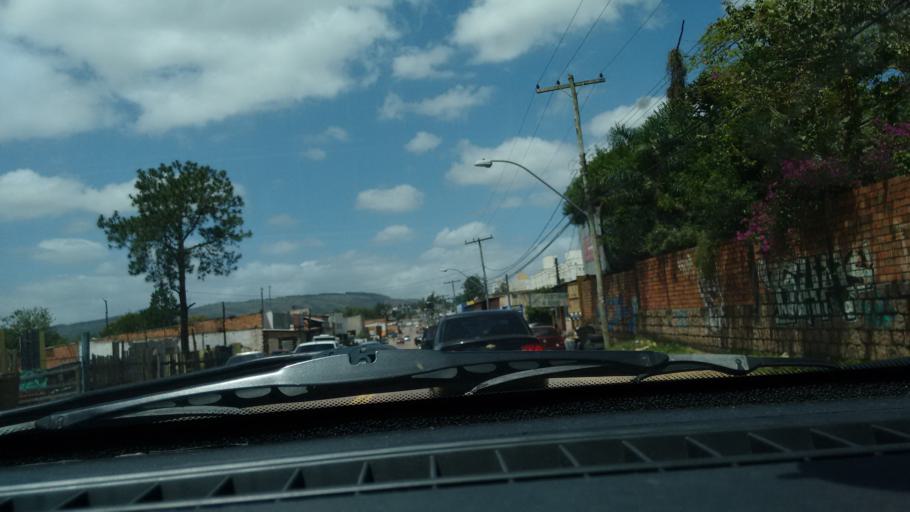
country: BR
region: Rio Grande do Sul
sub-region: Cachoeirinha
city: Cachoeirinha
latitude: -30.0068
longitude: -51.1278
